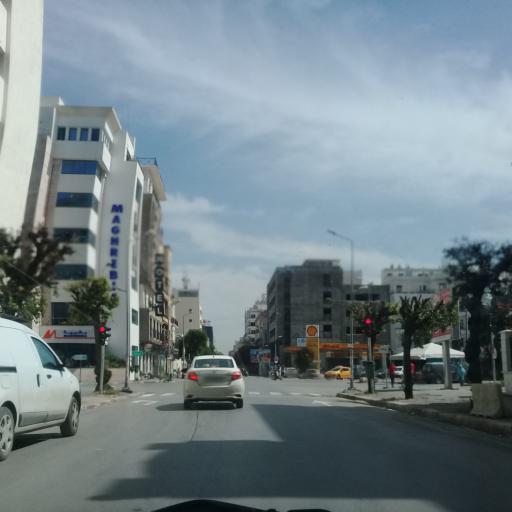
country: TN
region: Tunis
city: Tunis
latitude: 36.8157
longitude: 10.1790
